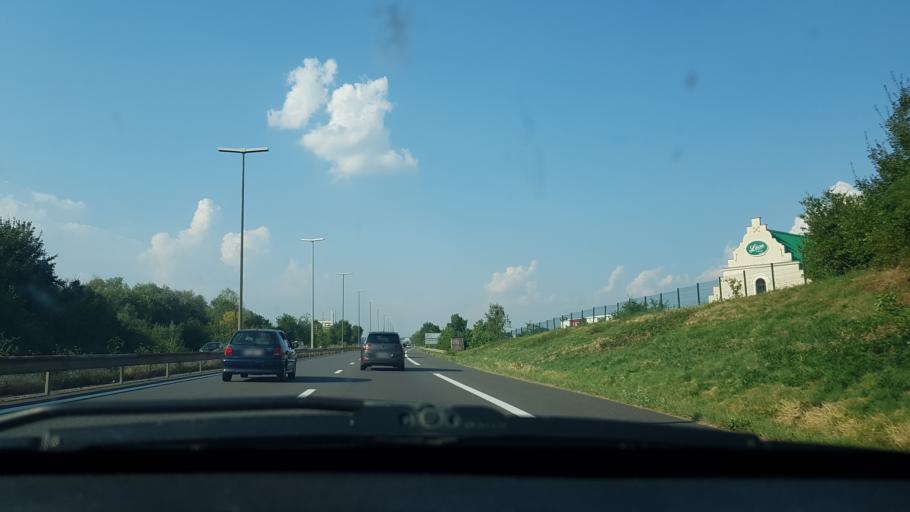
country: FR
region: Lorraine
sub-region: Departement de Meurthe-et-Moselle
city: Vandoeuvre-les-Nancy
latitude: 48.6529
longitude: 6.1826
